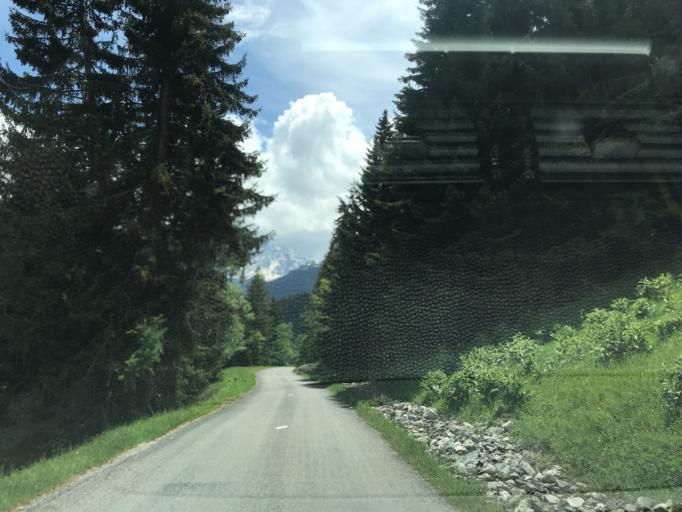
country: FR
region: Rhone-Alpes
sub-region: Departement de la Savoie
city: Modane
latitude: 45.2175
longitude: 6.6492
